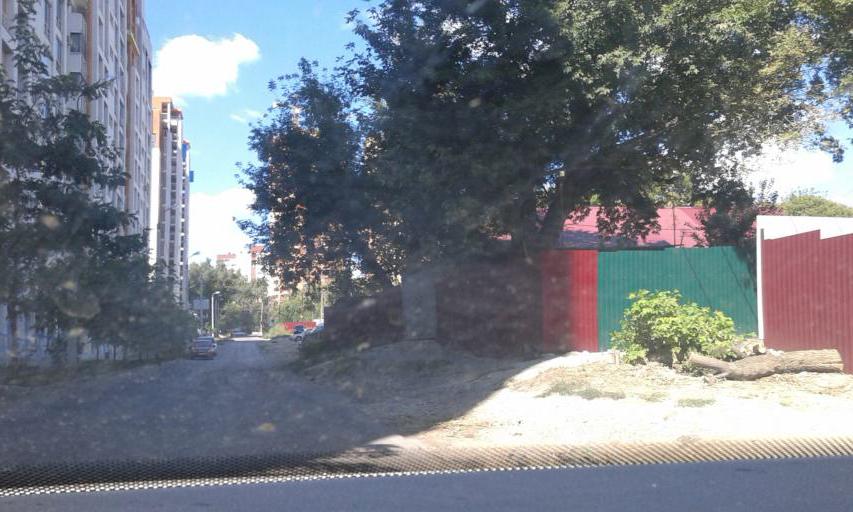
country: RU
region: Volgograd
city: Volgograd
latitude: 48.6776
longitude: 44.4797
